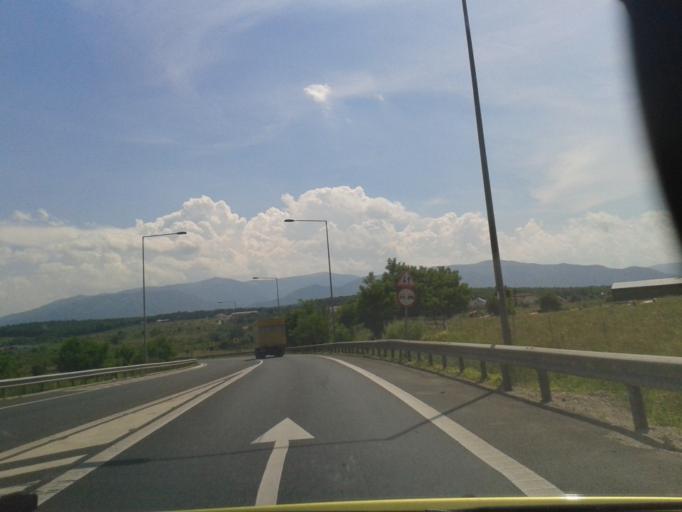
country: RO
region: Sibiu
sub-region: Comuna Selimbar
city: Selimbar
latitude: 45.7482
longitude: 24.2007
